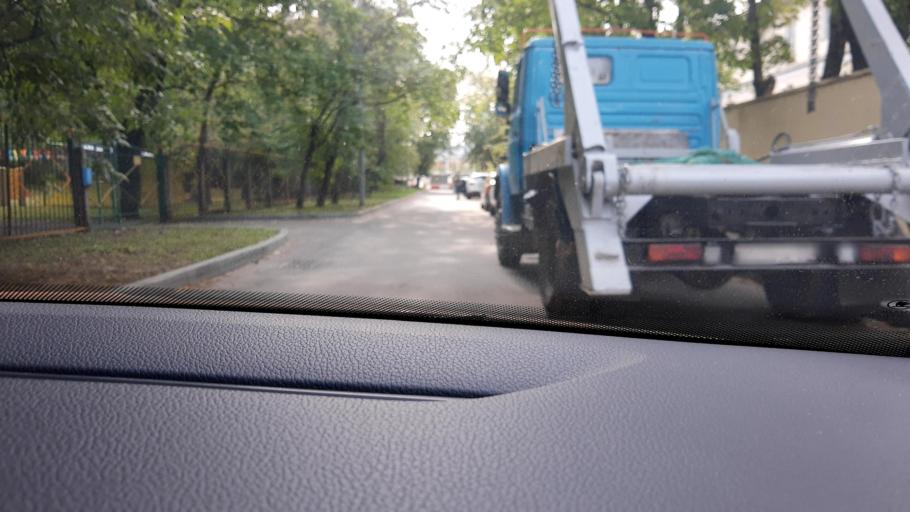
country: RU
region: Moskovskaya
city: Kur'yanovo
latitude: 55.6521
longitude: 37.7005
